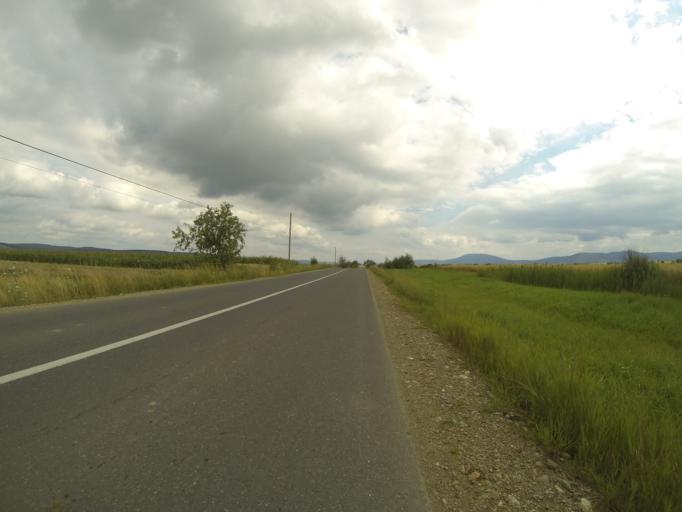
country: RO
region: Brasov
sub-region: Comuna Parau
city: Parau
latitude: 45.8512
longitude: 25.1930
